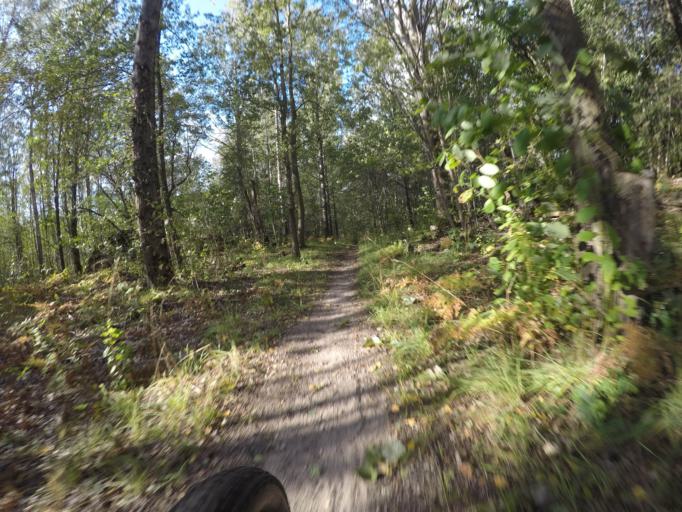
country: SE
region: Vaestmanland
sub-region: Kopings Kommun
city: Koping
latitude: 59.5070
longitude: 16.0205
